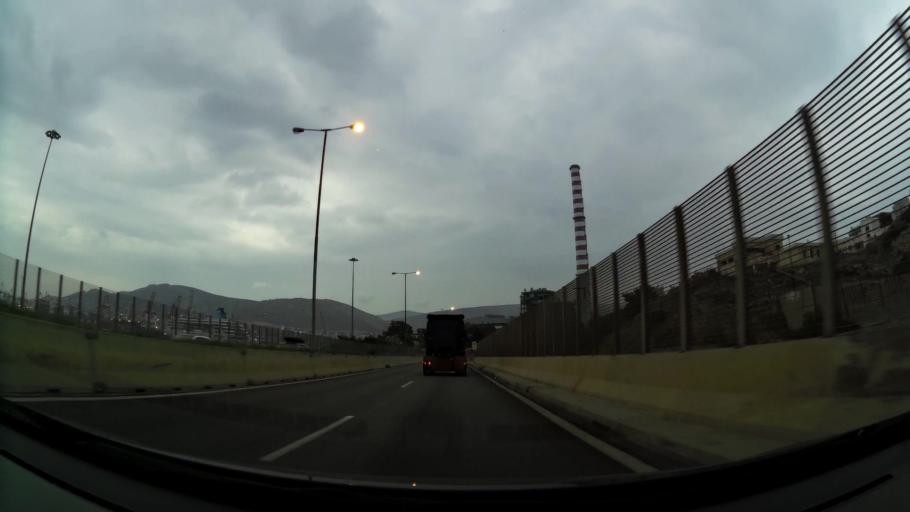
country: GR
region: Attica
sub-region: Nomos Piraios
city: Drapetsona
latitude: 37.9506
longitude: 23.6095
